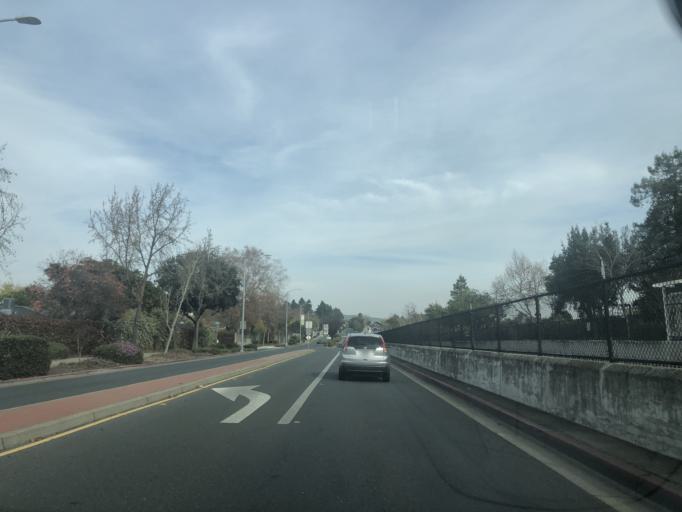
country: US
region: California
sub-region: Contra Costa County
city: Concord
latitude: 37.9986
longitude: -122.0284
